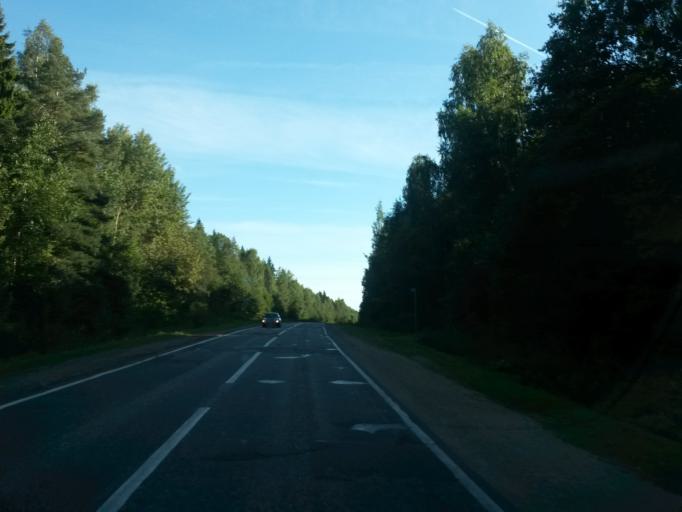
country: RU
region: Jaroslavl
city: Krasnyye Tkachi
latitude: 57.4731
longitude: 39.9081
